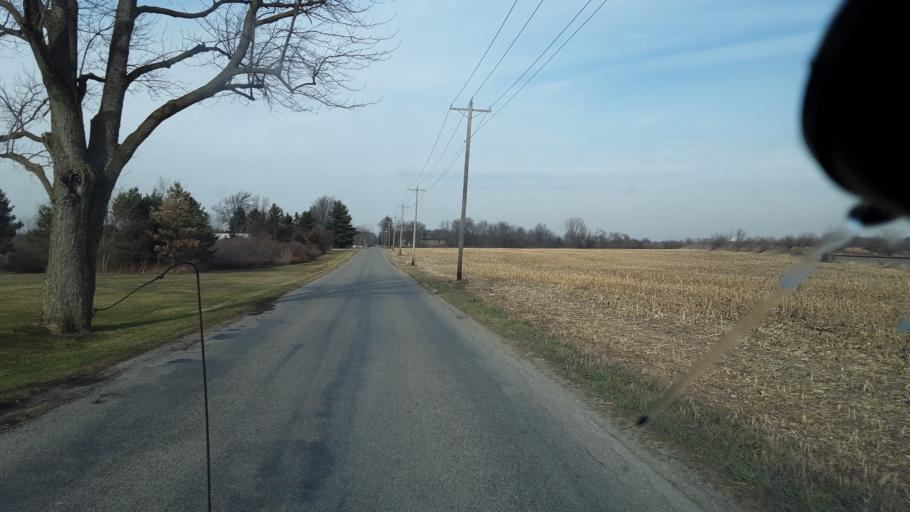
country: US
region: Indiana
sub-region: DeKalb County
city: Butler
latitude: 41.4003
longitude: -84.8892
